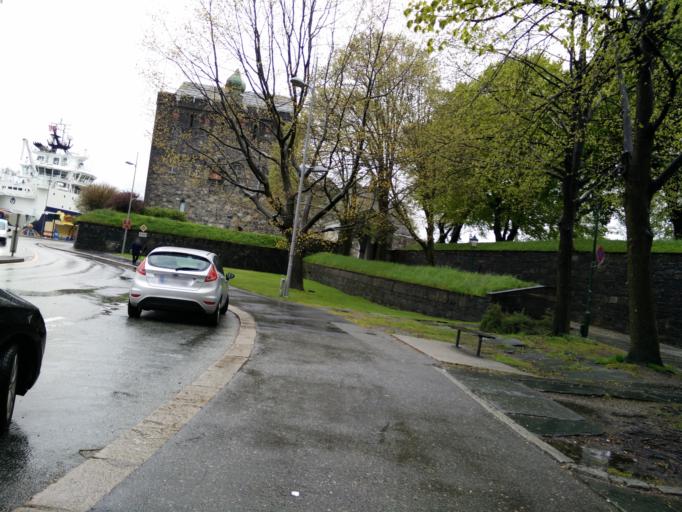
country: NO
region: Hordaland
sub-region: Bergen
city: Bergen
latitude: 60.3987
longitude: 5.3199
